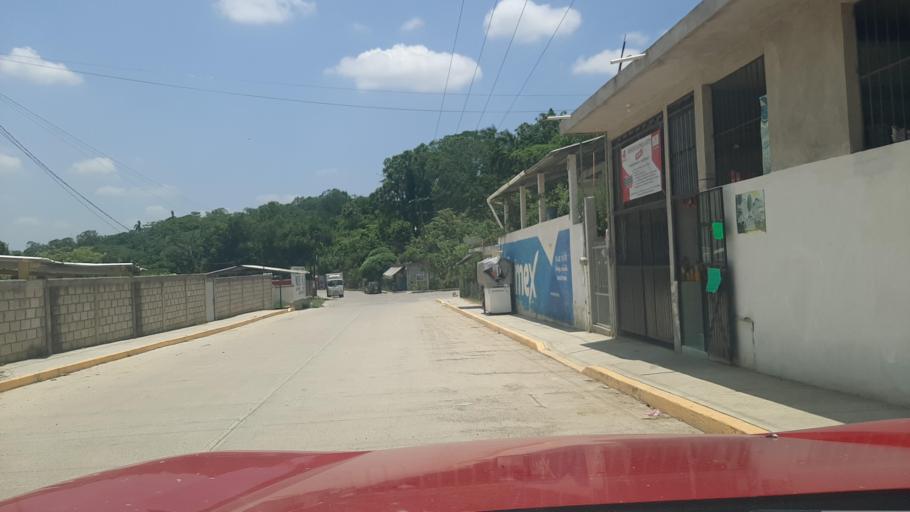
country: MX
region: Veracruz
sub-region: Poza Rica de Hidalgo
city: Arroyo del Maiz Uno
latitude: 20.4983
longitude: -97.4242
